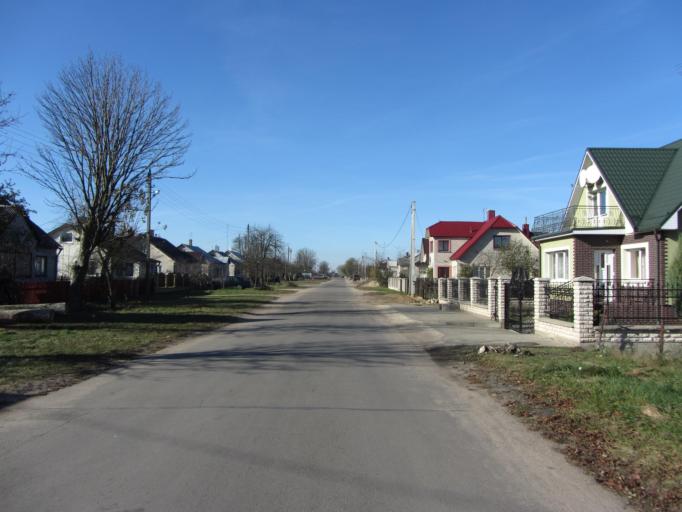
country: LT
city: Eisiskes
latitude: 54.1639
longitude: 25.0016
